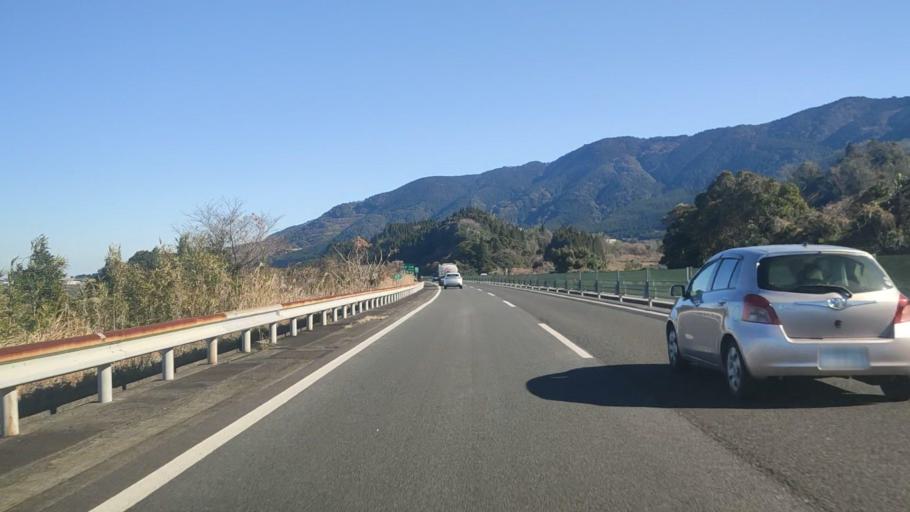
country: JP
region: Miyazaki
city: Miyazaki-shi
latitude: 31.8199
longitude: 131.2935
